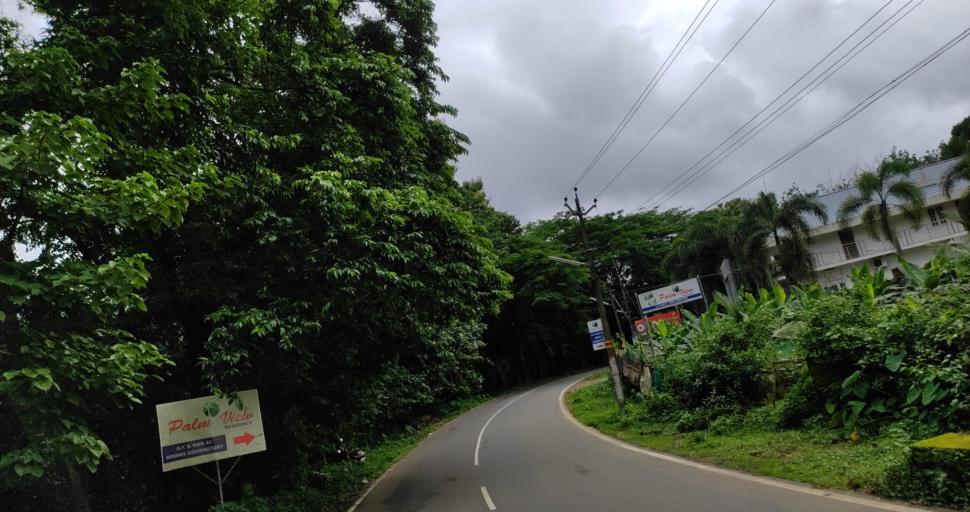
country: IN
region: Kerala
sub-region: Ernakulam
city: Angamali
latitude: 10.2944
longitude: 76.4832
